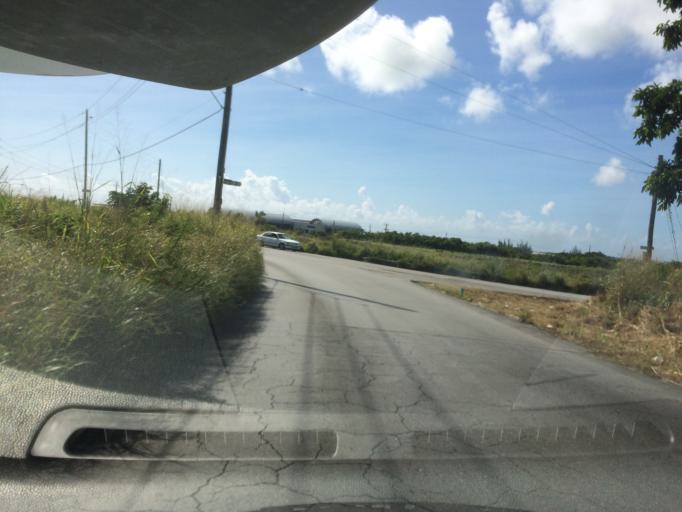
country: BB
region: Christ Church
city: Oistins
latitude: 13.0817
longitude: -59.5293
